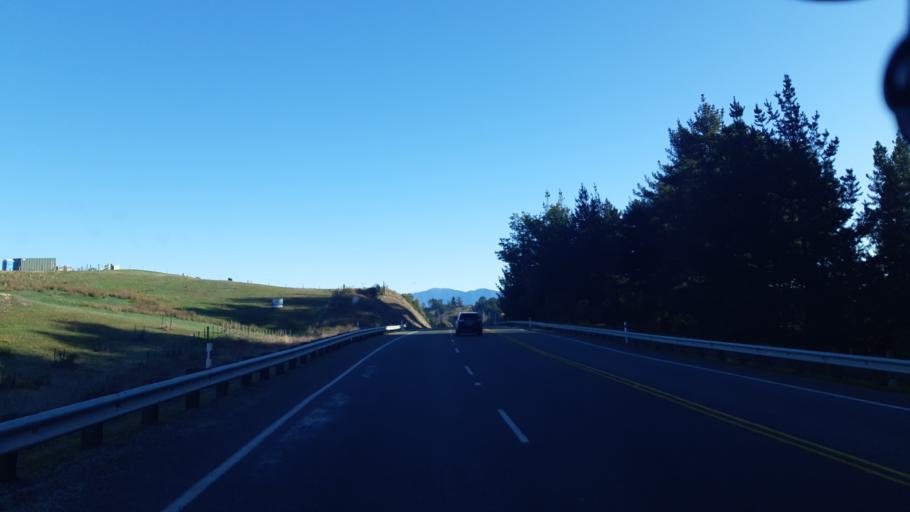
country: NZ
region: Tasman
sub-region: Tasman District
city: Mapua
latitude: -41.2848
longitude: 173.0792
